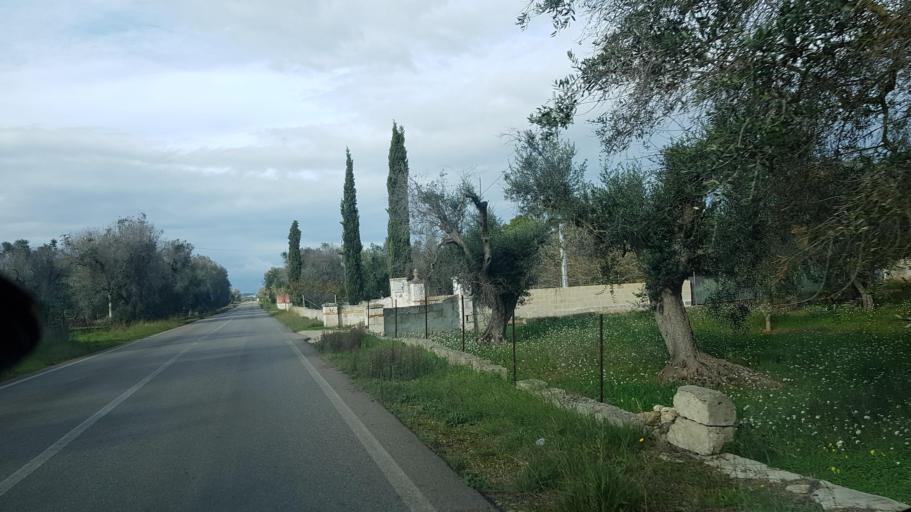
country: IT
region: Apulia
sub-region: Provincia di Brindisi
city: Torre Santa Susanna
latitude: 40.4761
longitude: 17.7008
